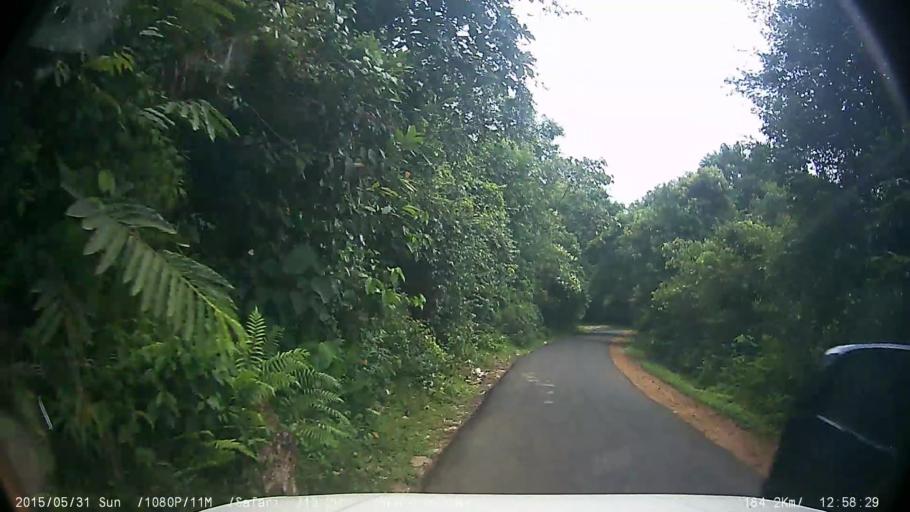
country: IN
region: Kerala
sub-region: Wayanad
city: Kalpetta
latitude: 11.5102
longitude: 76.1372
